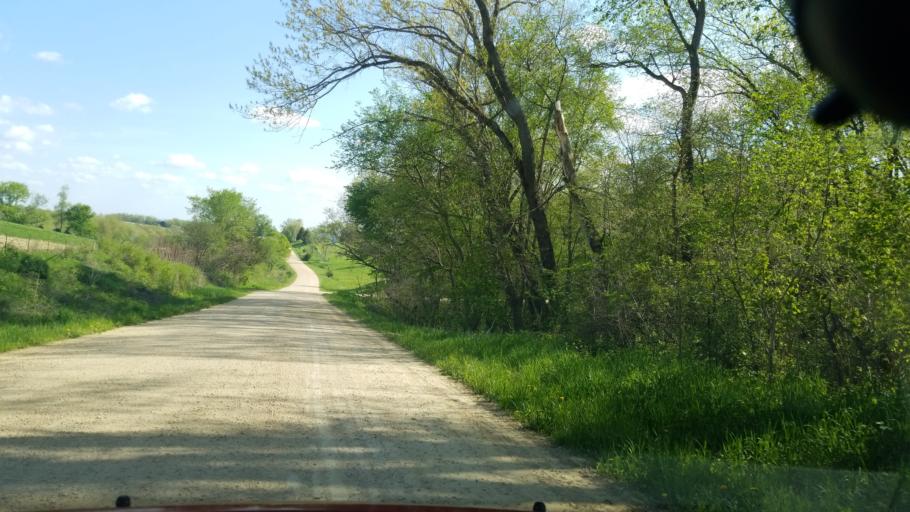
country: US
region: Iowa
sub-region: Jackson County
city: Maquoketa
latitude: 42.1980
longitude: -90.7295
